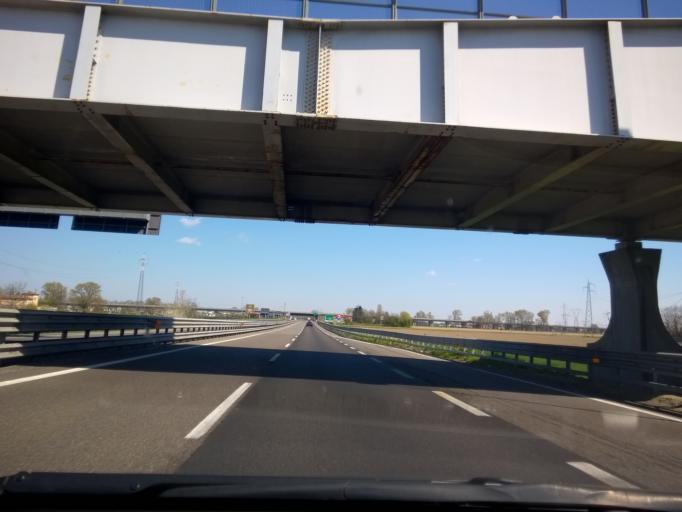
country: IT
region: Emilia-Romagna
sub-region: Provincia di Piacenza
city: Piacenza
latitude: 45.0514
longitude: 9.7546
